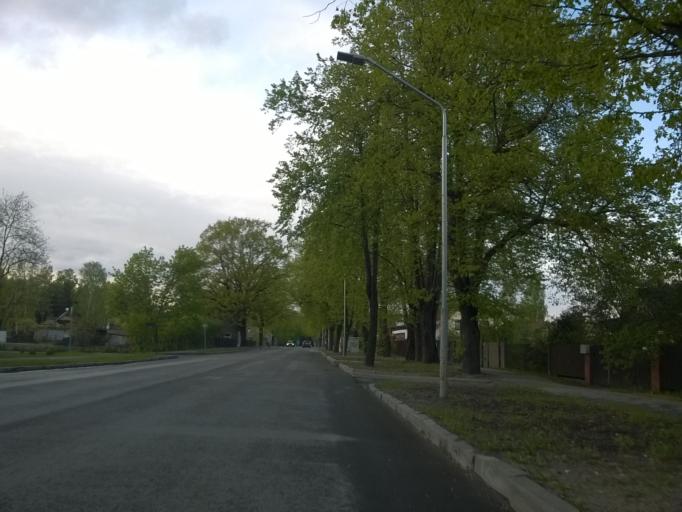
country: LV
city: Tireli
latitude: 56.9513
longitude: 23.6331
